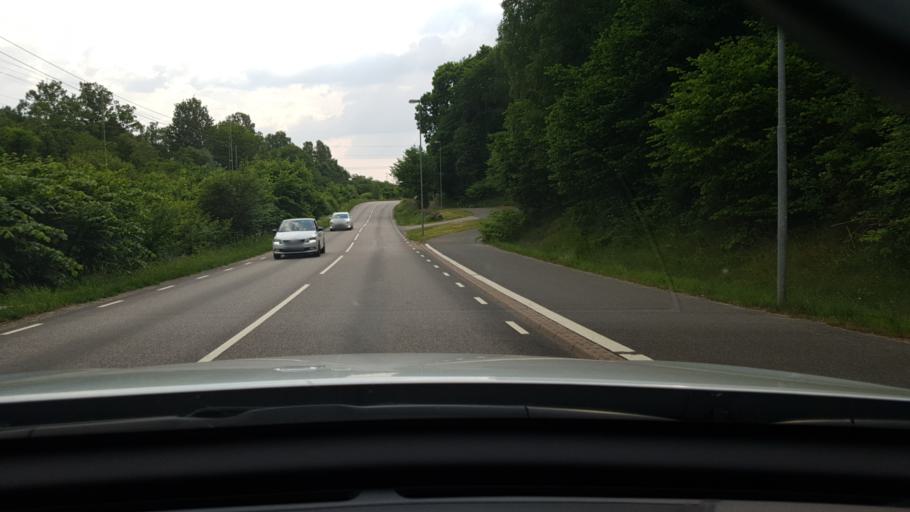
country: SE
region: Vaestra Goetaland
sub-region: Lerums Kommun
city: Stenkullen
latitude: 57.8052
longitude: 12.3502
